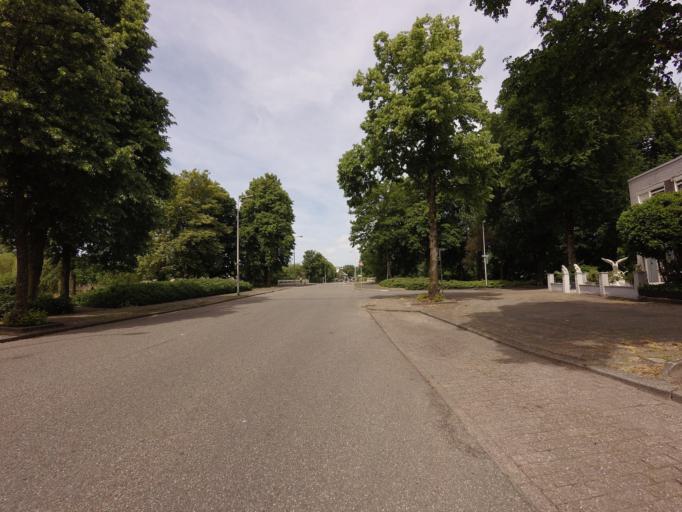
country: NL
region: Utrecht
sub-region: Gemeente Utrecht
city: Utrecht
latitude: 52.1209
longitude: 5.0943
